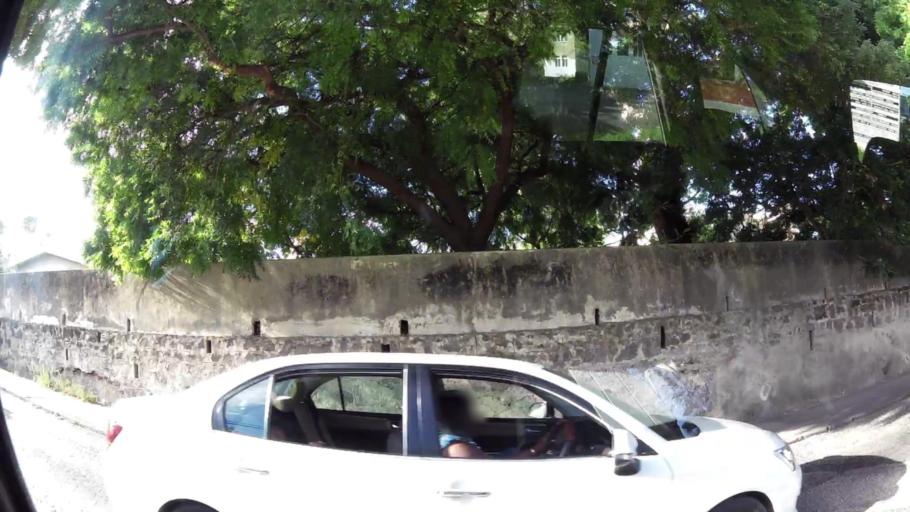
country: BB
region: Saint Michael
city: Bridgetown
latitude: 13.0927
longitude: -59.5909
